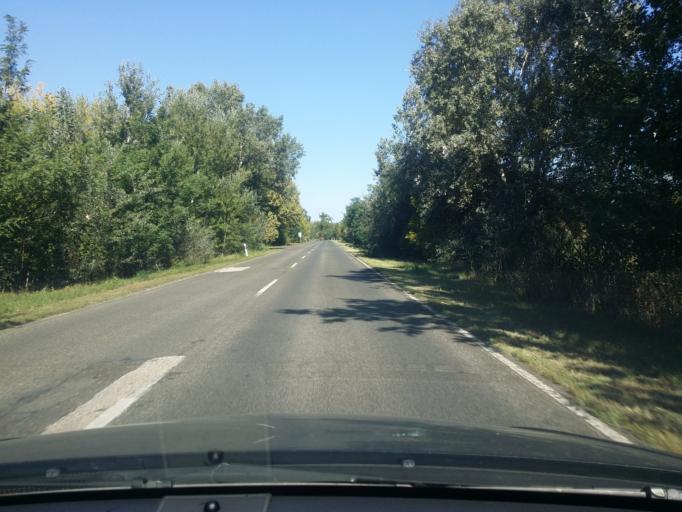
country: HU
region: Csongrad
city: Kistelek
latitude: 46.5099
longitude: 19.9673
